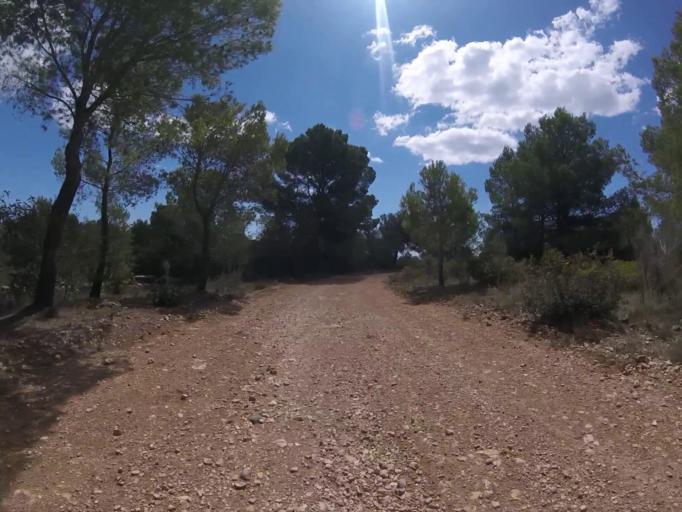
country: ES
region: Valencia
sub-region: Provincia de Castello
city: Alcoceber
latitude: 40.2858
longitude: 0.3229
